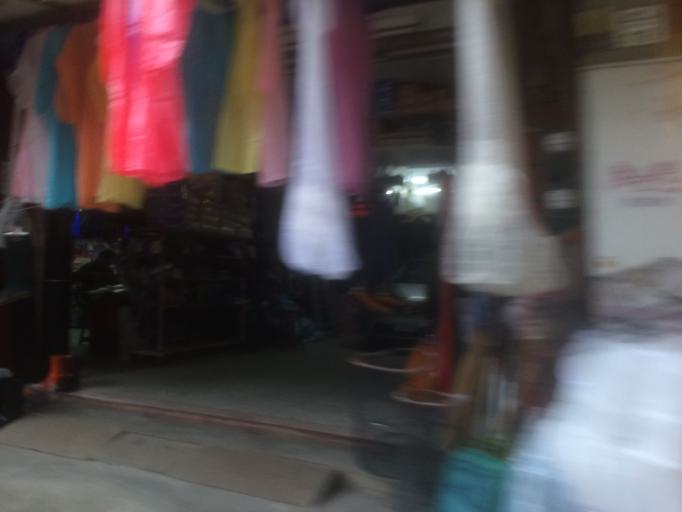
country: TW
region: Taiwan
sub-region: Yilan
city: Yilan
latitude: 24.6746
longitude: 121.7710
